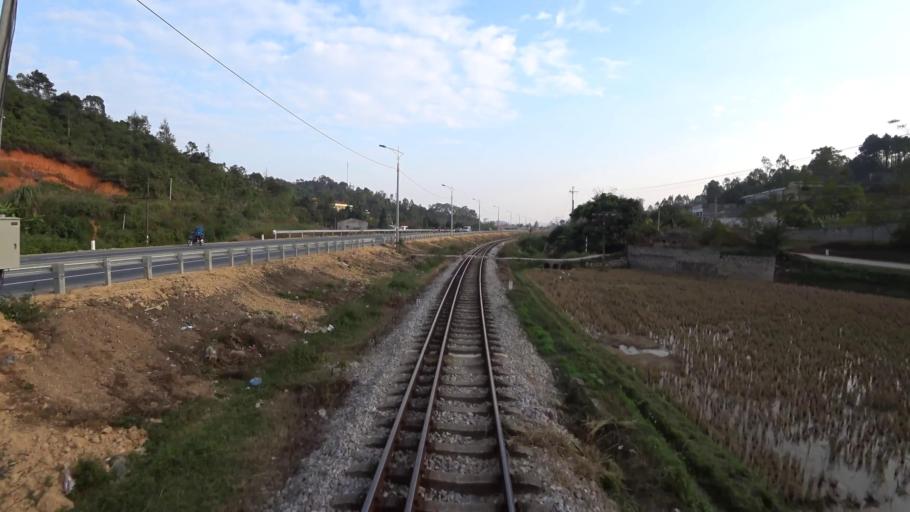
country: VN
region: Lang Son
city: Thi Tran Cao Loc
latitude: 21.8999
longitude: 106.7401
